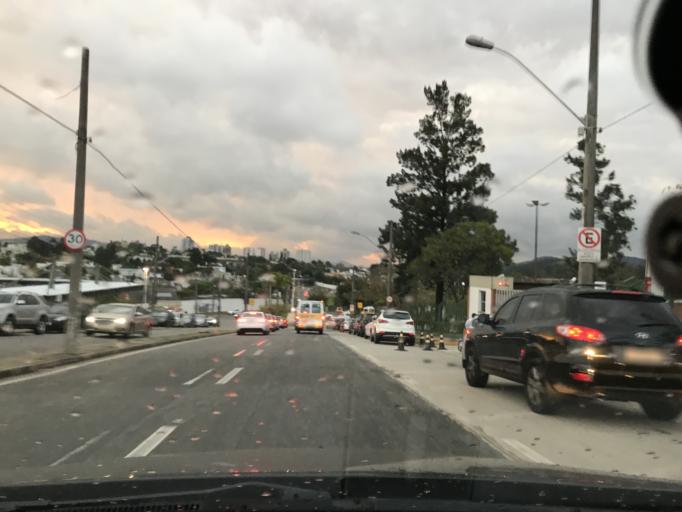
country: BR
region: Sao Paulo
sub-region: Carapicuiba
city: Carapicuiba
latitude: -23.4883
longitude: -46.8325
